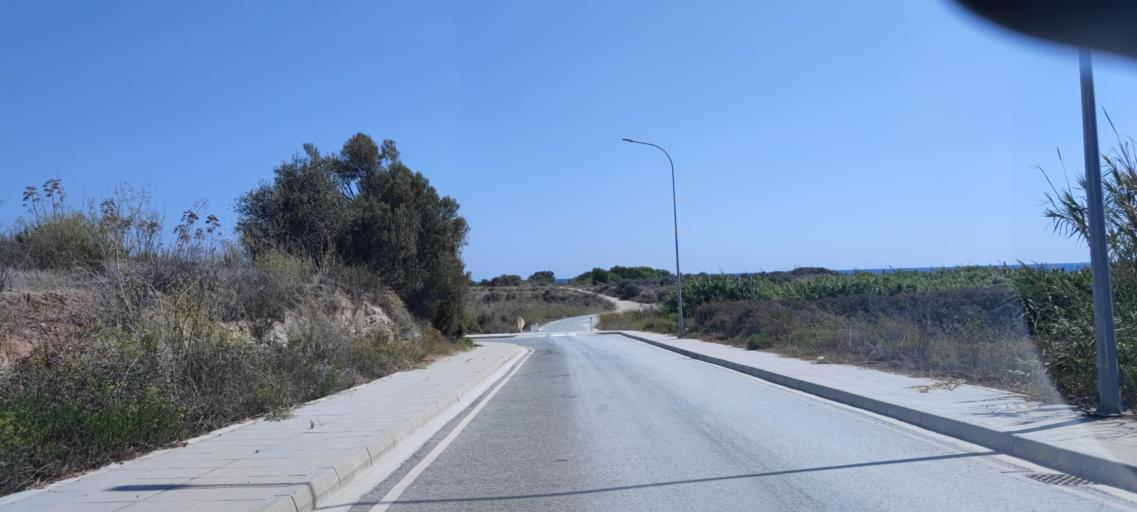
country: CY
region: Larnaka
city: Kofinou
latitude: 34.7779
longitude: 33.4679
